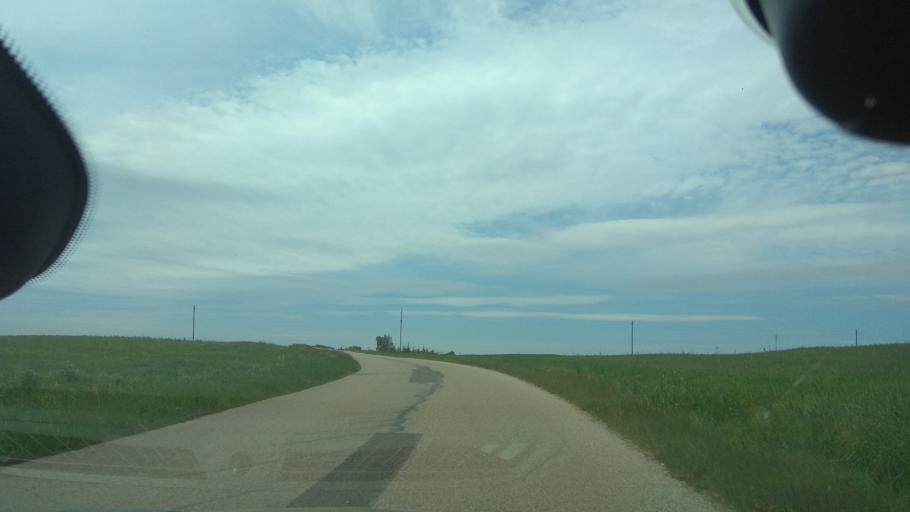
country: LT
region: Vilnius County
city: Ukmerge
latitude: 55.1615
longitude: 24.5339
